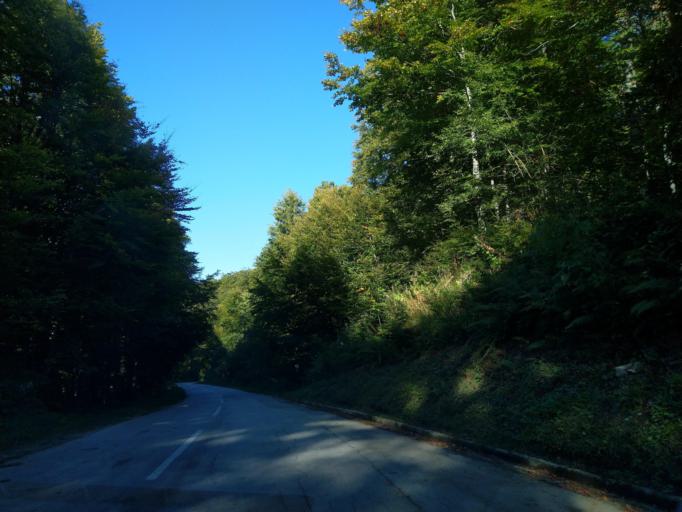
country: RS
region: Central Serbia
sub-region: Moravicki Okrug
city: Ivanjica
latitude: 43.4377
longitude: 20.2693
